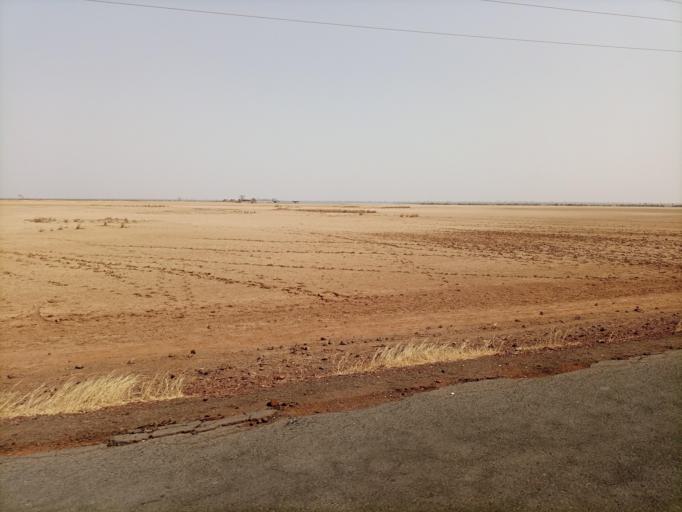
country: SN
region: Fatick
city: Foundiougne
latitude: 14.1698
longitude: -16.4617
